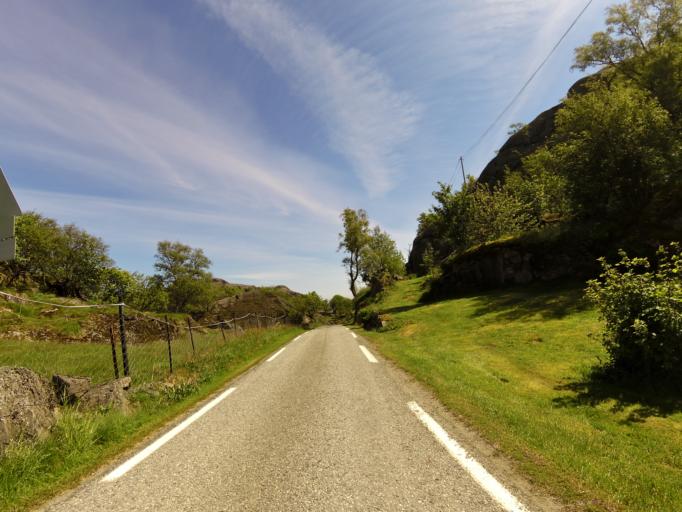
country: NO
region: Rogaland
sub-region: Sokndal
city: Hauge i Dalane
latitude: 58.3565
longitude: 6.1556
